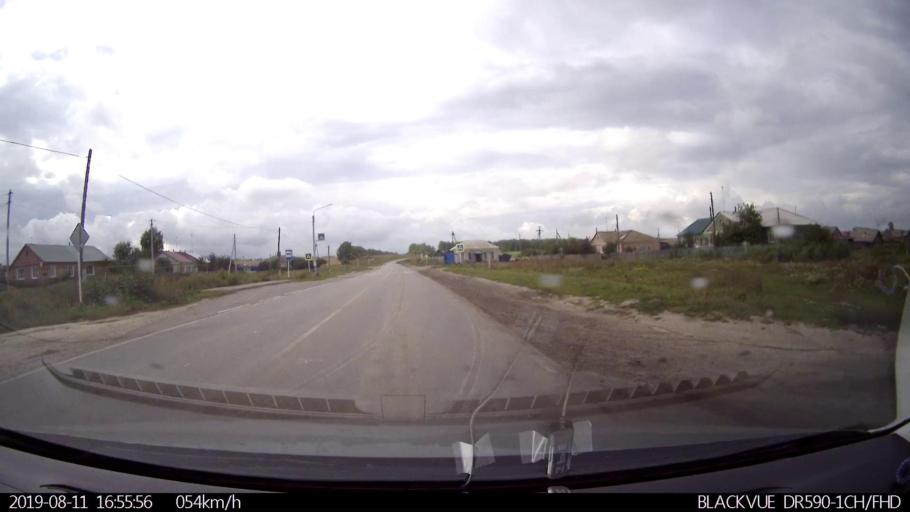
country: RU
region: Ulyanovsk
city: Mayna
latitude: 54.2847
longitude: 47.6586
